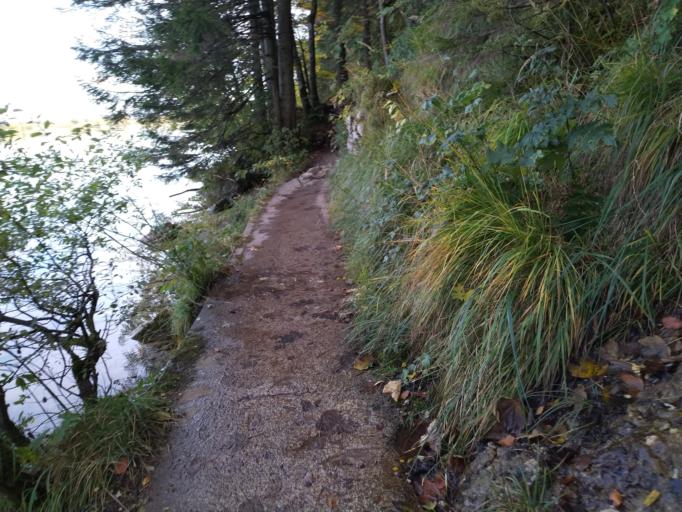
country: AT
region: Tyrol
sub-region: Politischer Bezirk Reutte
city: Vils
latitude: 47.5675
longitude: 10.6328
